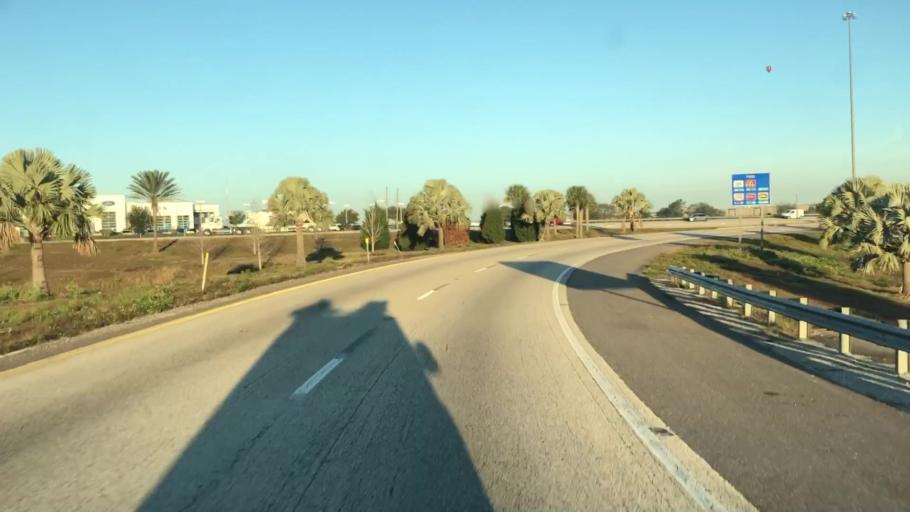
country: US
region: Florida
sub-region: Polk County
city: Loughman
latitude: 28.2323
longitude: -81.6529
